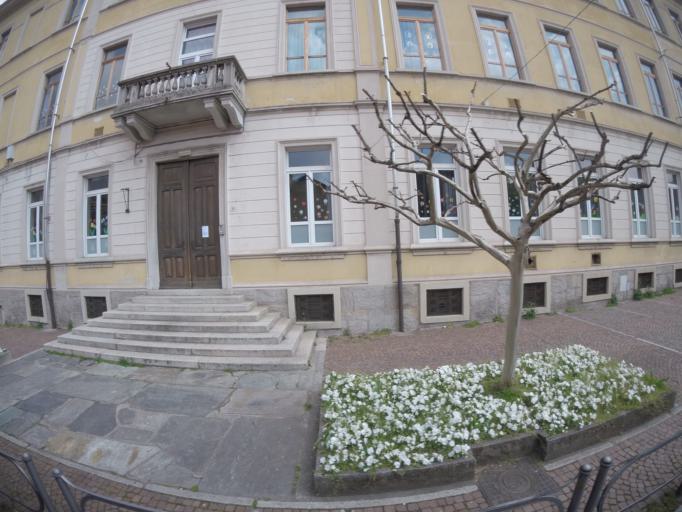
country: IT
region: Piedmont
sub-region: Provincia Verbano-Cusio-Ossola
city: Omegna
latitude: 45.8764
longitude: 8.4109
